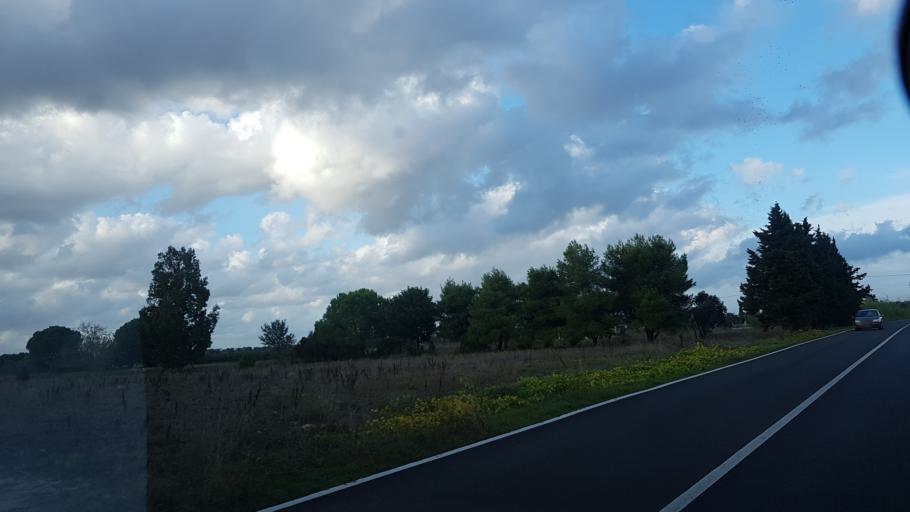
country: IT
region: Apulia
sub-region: Provincia di Brindisi
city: San Pietro Vernotico
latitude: 40.5099
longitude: 18.0092
